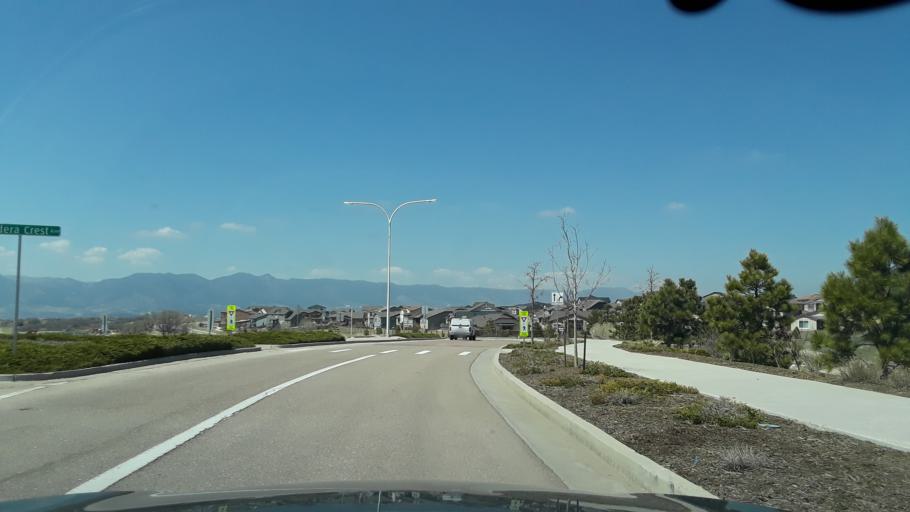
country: US
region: Colorado
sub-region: El Paso County
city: Black Forest
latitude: 38.9775
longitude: -104.7448
